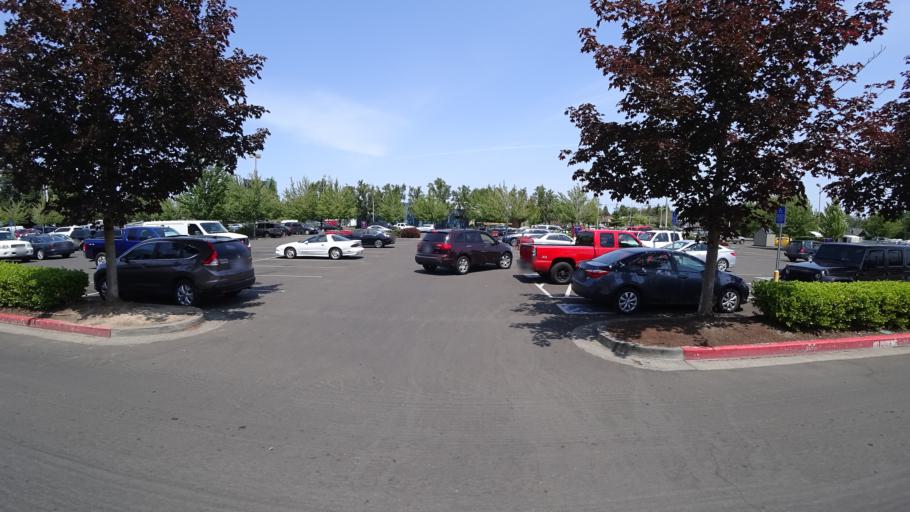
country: US
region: Oregon
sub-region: Washington County
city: Hillsboro
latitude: 45.5035
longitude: -122.9573
